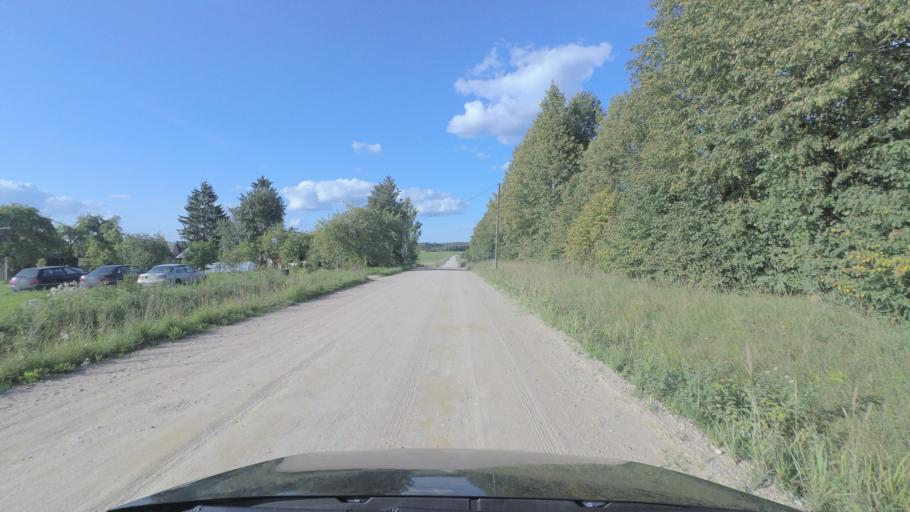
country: LT
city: Pabrade
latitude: 55.1295
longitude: 25.7054
